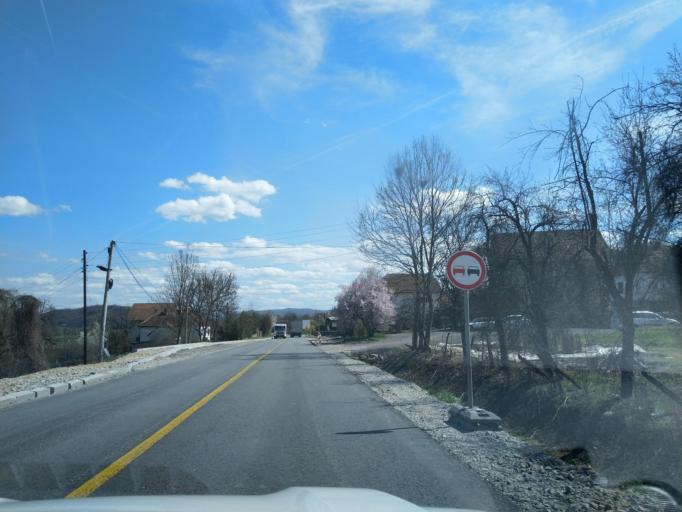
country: RS
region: Central Serbia
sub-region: Zlatiborski Okrug
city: Pozega
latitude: 43.8286
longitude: 20.0763
